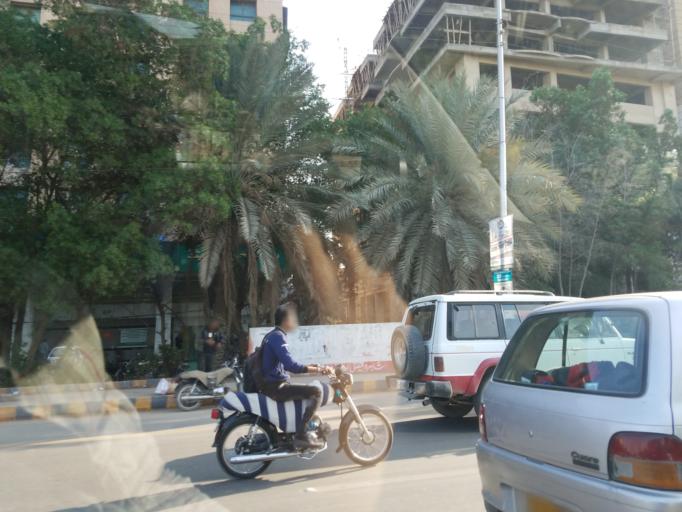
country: PK
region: Sindh
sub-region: Karachi District
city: Karachi
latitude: 24.8615
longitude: 67.0677
